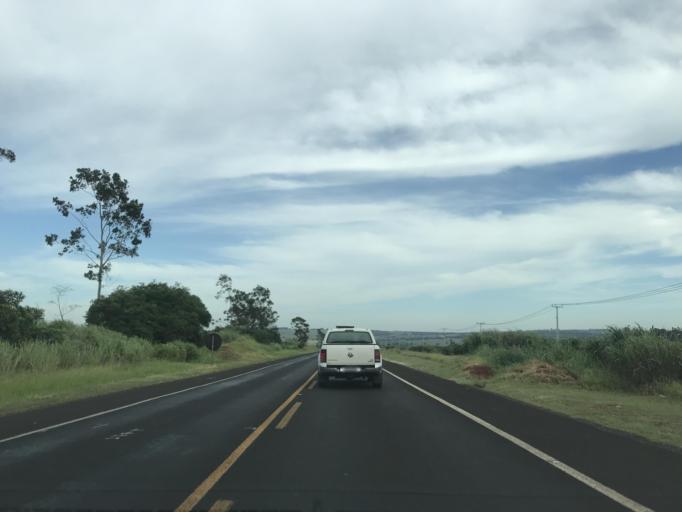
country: BR
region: Parana
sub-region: Paranavai
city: Paranavai
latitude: -23.0126
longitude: -52.5359
